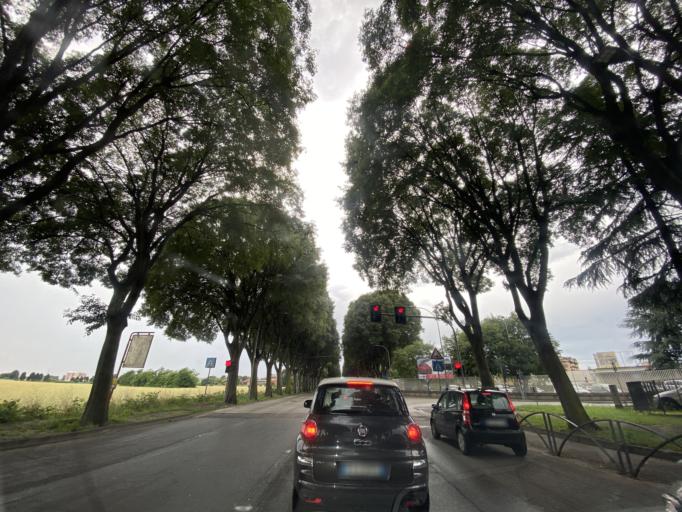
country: IT
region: Lombardy
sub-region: Provincia di Monza e Brianza
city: Monza
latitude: 45.5666
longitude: 9.2561
